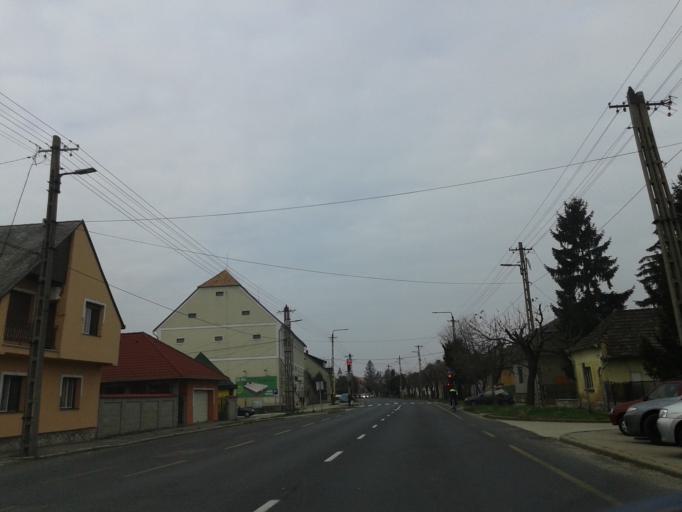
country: HU
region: Komarom-Esztergom
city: Komarom
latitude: 47.7349
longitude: 18.1767
